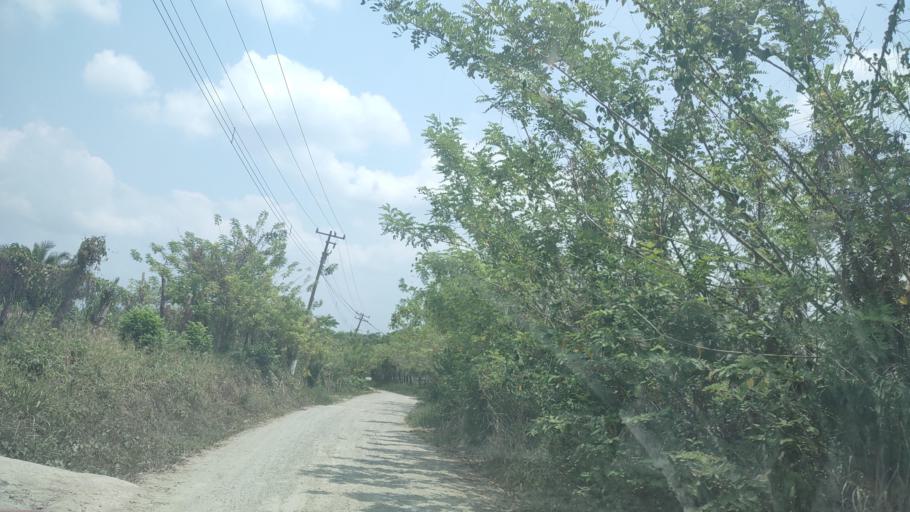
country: MX
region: Tabasco
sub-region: Huimanguillo
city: Francisco Rueda
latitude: 17.5840
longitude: -93.9593
